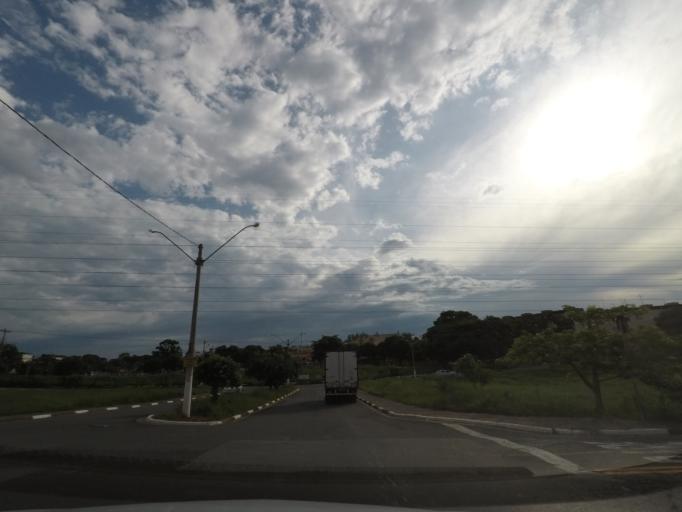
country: BR
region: Sao Paulo
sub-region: Campinas
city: Campinas
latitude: -22.9073
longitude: -47.1139
